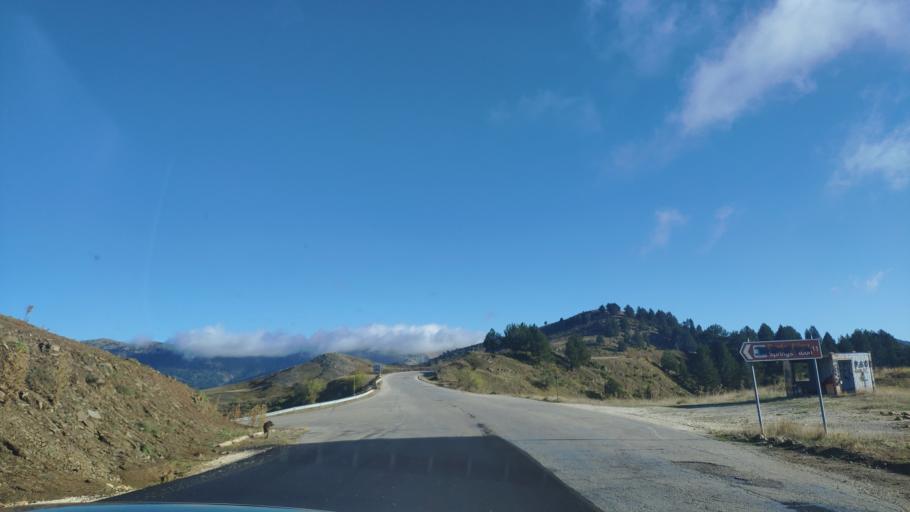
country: GR
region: Epirus
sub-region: Nomos Ioanninon
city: Metsovo
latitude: 39.7919
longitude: 21.1652
